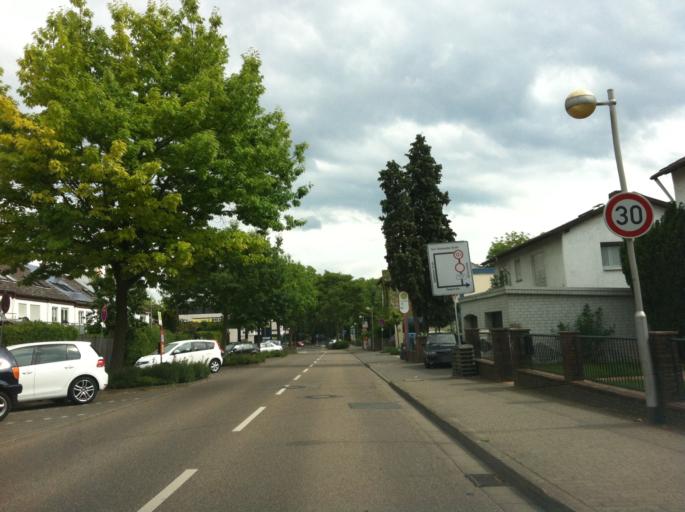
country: DE
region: Hesse
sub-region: Regierungsbezirk Darmstadt
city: Eschborn
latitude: 50.1440
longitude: 8.5743
